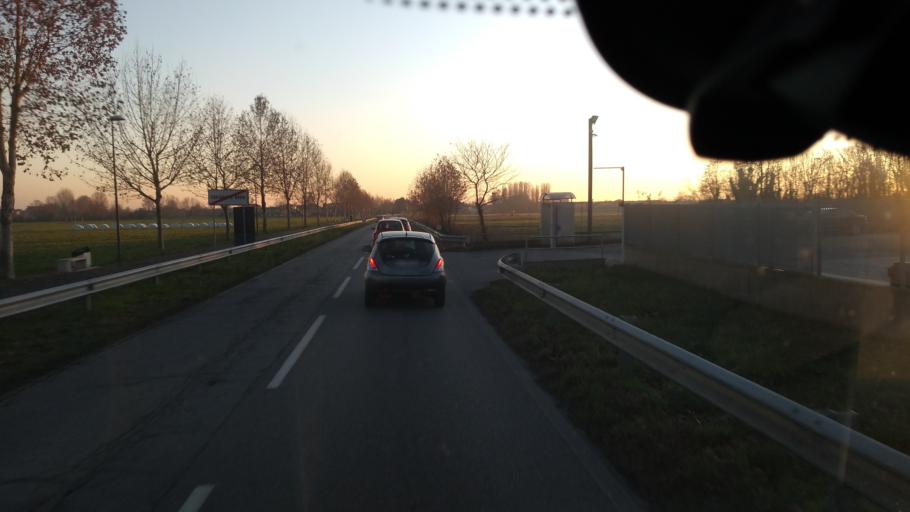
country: IT
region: Lombardy
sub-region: Provincia di Bergamo
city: Casirate d'Adda
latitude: 45.4892
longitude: 9.5666
